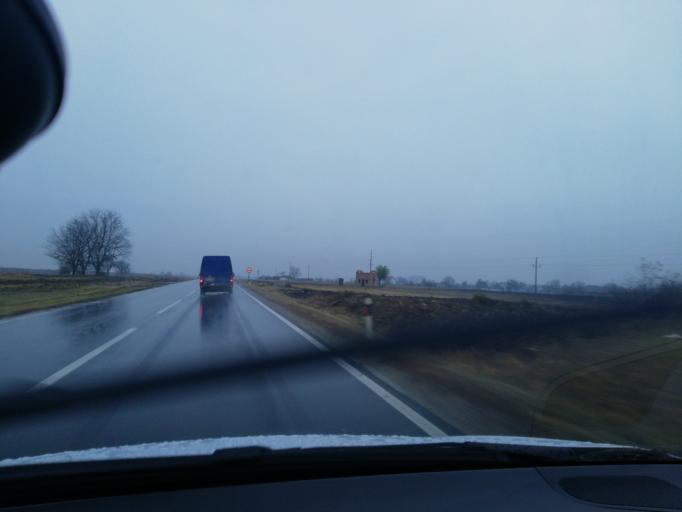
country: RS
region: Autonomna Pokrajina Vojvodina
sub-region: Sremski Okrug
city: Ruma
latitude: 45.0187
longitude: 19.8402
